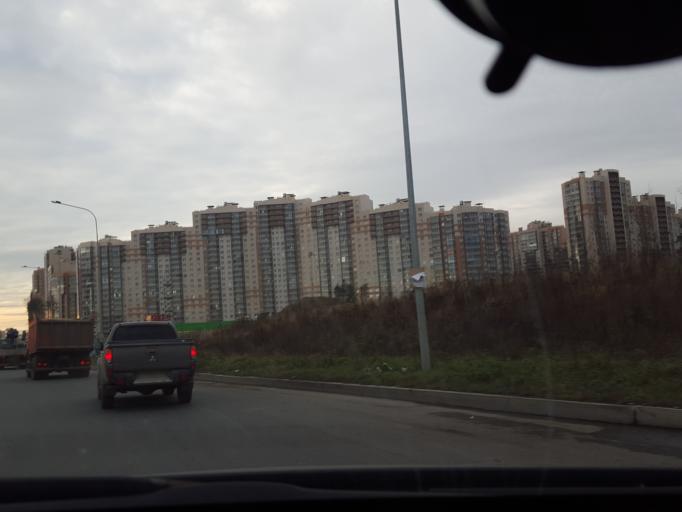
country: RU
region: St.-Petersburg
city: Kolomyagi
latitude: 60.0330
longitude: 30.2532
